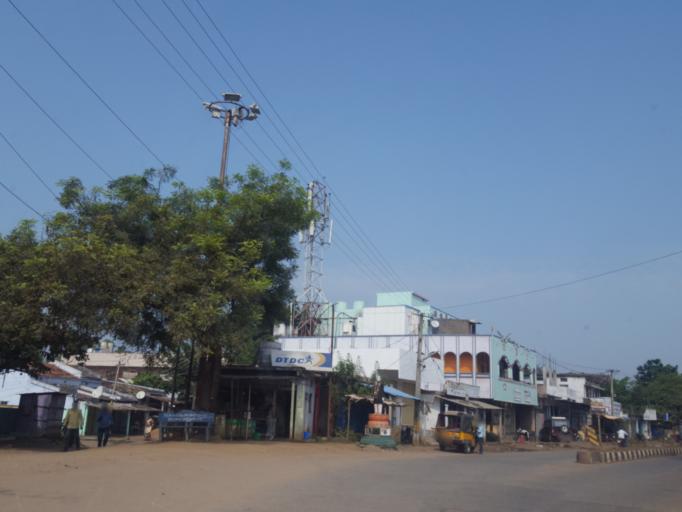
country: IN
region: Telangana
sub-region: Khammam
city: Yellandu
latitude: 17.5914
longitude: 80.3201
